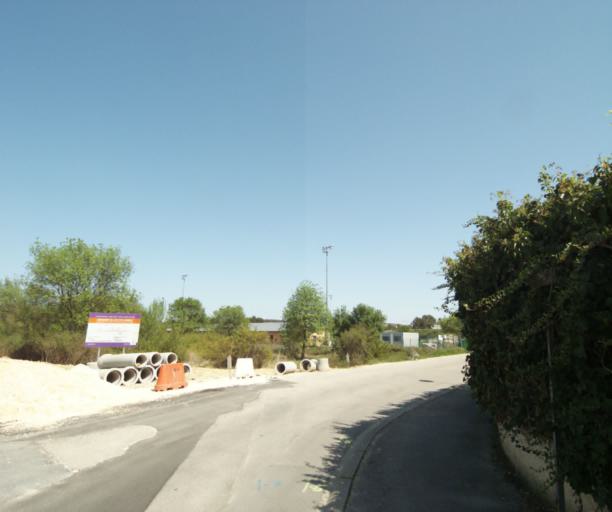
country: FR
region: Languedoc-Roussillon
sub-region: Departement de l'Herault
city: Grabels
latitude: 43.6525
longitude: 3.8095
